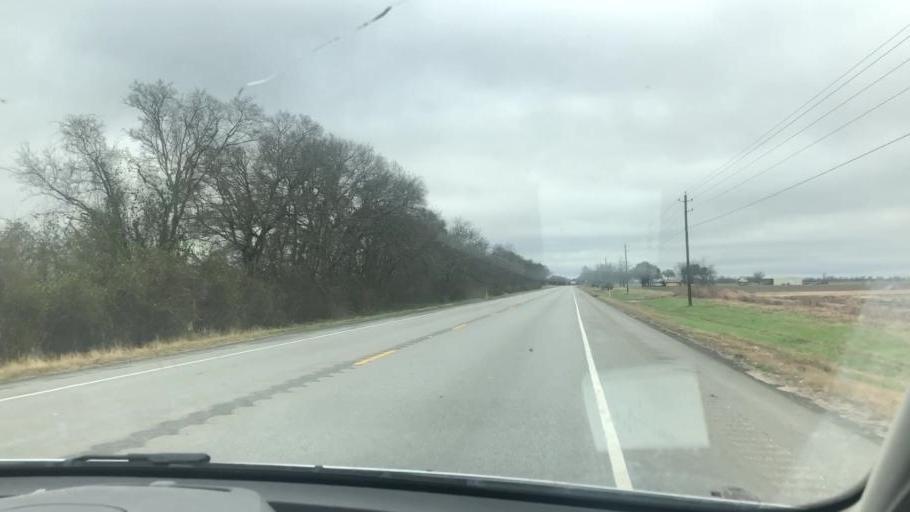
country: US
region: Texas
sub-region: Matagorda County
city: Bay City
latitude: 29.0727
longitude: -95.9720
